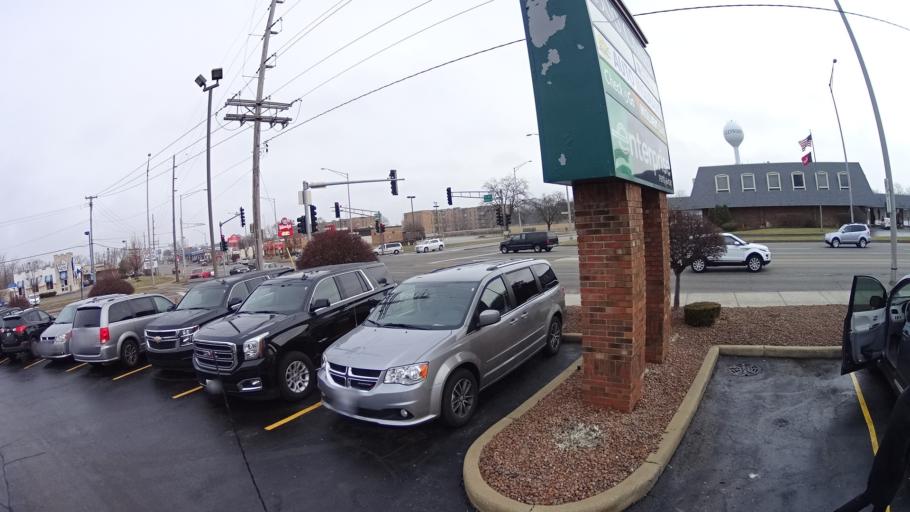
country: US
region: Illinois
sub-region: Cook County
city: East Hazel Crest
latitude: 41.5571
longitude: -87.6363
